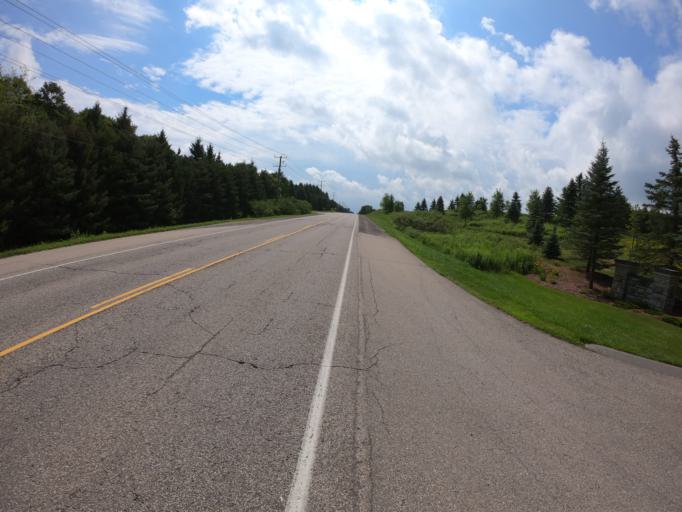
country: CA
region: Ontario
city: Waterloo
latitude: 43.4546
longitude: -80.6513
